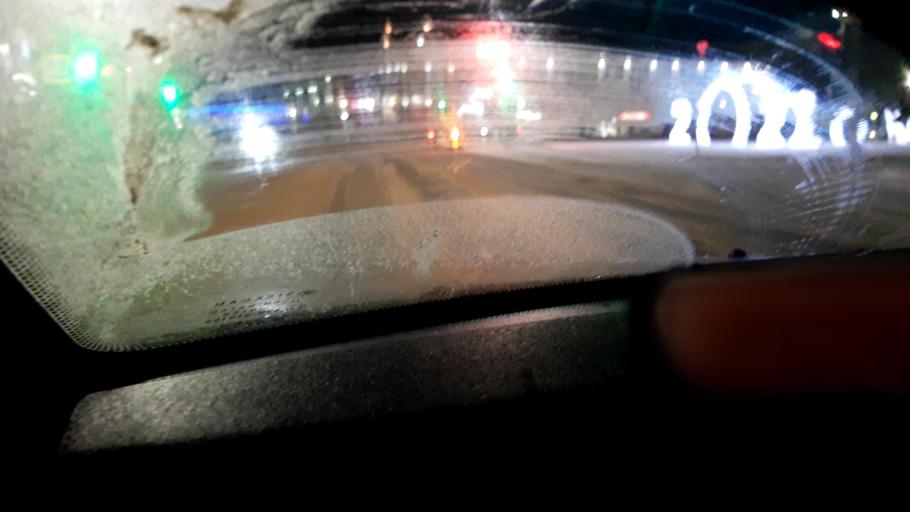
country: RU
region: Nizjnij Novgorod
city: Bogorodsk
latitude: 56.1037
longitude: 43.5158
